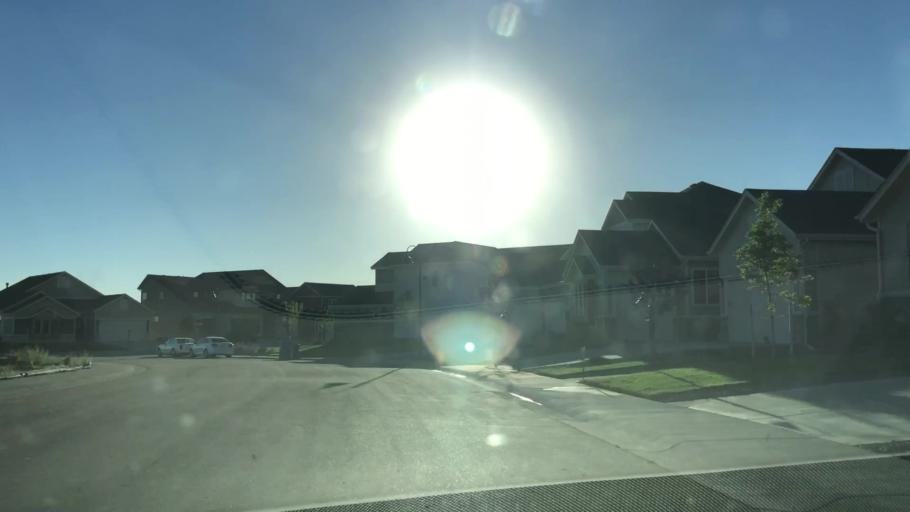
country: US
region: Colorado
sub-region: Larimer County
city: Loveland
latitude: 40.4209
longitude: -105.0171
